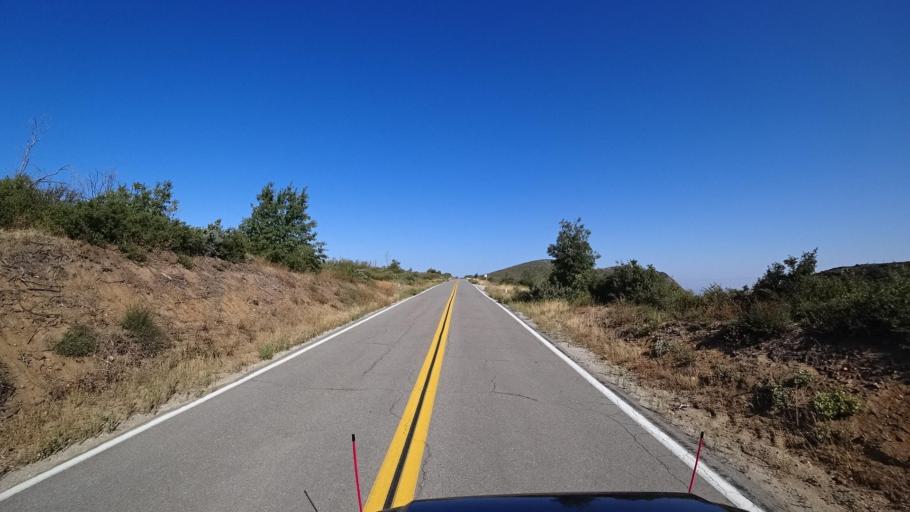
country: US
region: California
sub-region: San Diego County
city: Pine Valley
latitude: 32.8995
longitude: -116.4538
